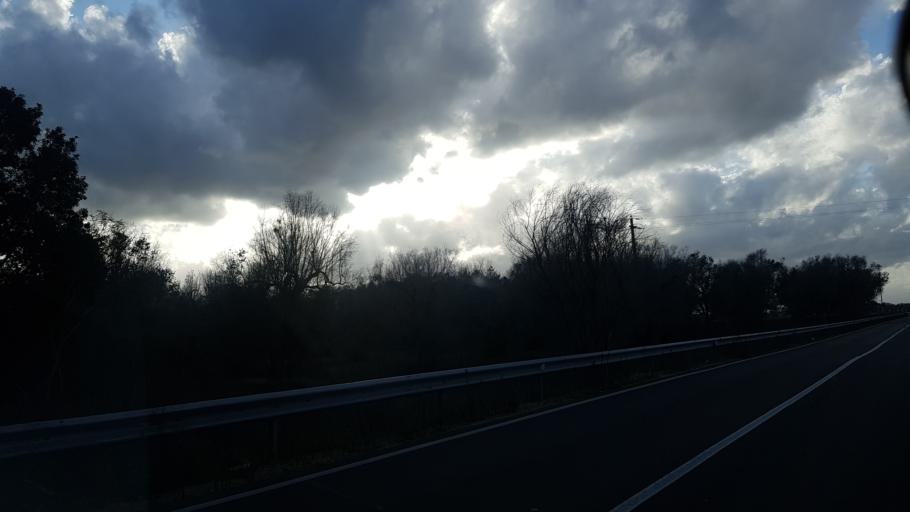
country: IT
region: Apulia
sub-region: Provincia di Brindisi
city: Torchiarolo
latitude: 40.4872
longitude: 18.0256
